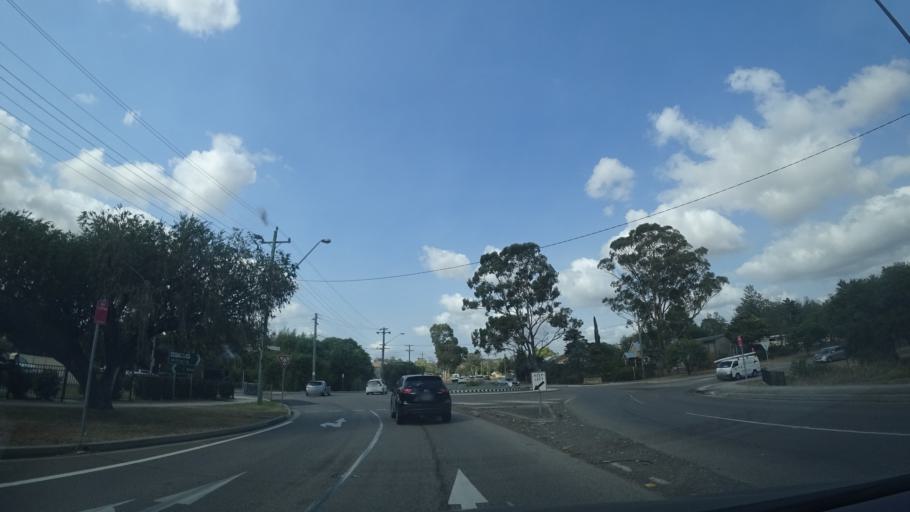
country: AU
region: New South Wales
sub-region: Wollondilly
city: Picton
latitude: -34.1854
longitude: 150.6065
